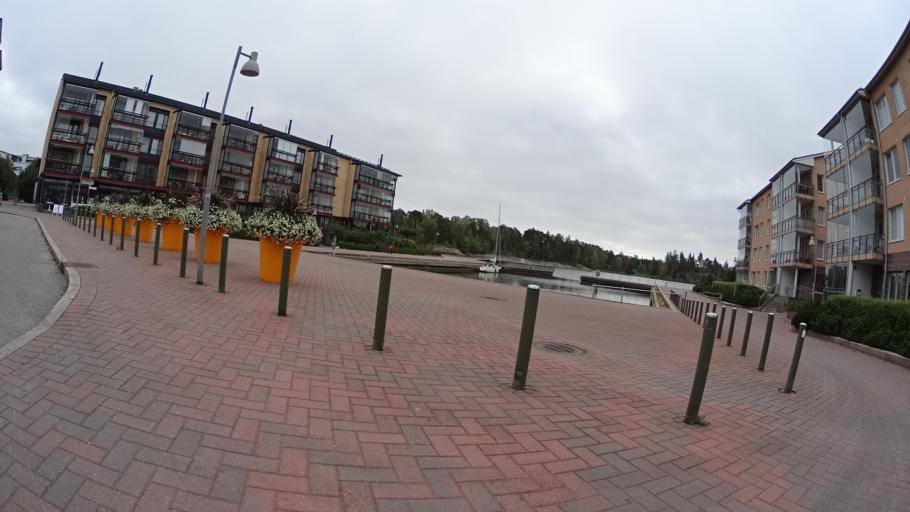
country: FI
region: Uusimaa
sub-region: Helsinki
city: Helsinki
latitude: 60.1857
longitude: 25.0322
